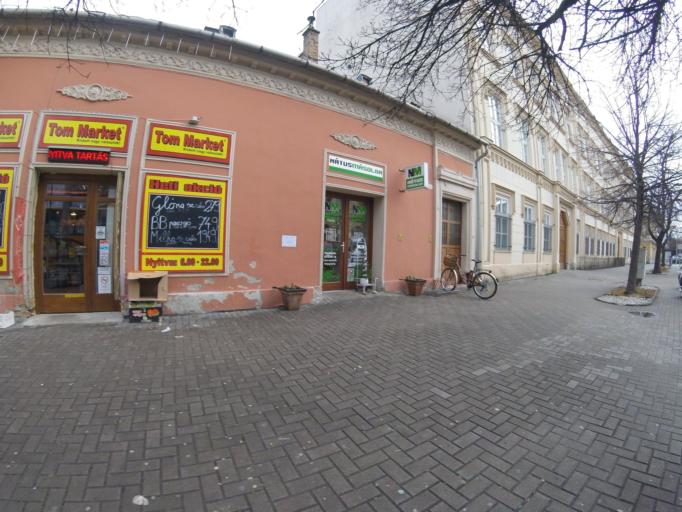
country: HU
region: Veszprem
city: Papa
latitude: 47.3290
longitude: 17.4692
